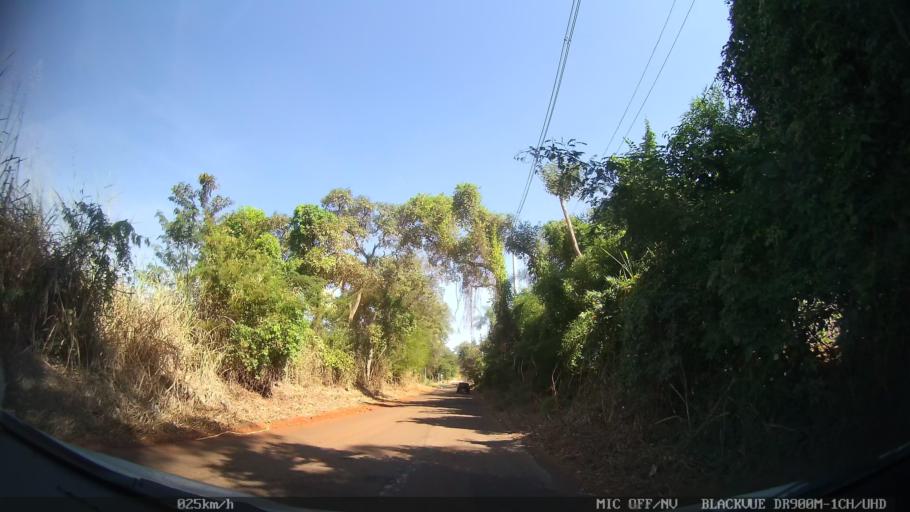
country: BR
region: Sao Paulo
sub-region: Ribeirao Preto
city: Ribeirao Preto
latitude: -21.2164
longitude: -47.8372
